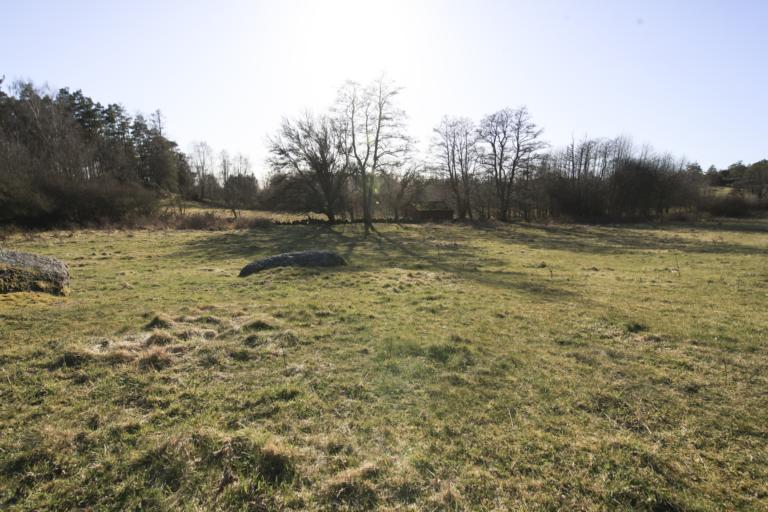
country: SE
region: Halland
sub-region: Varbergs Kommun
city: Varberg
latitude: 57.1683
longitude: 12.2659
